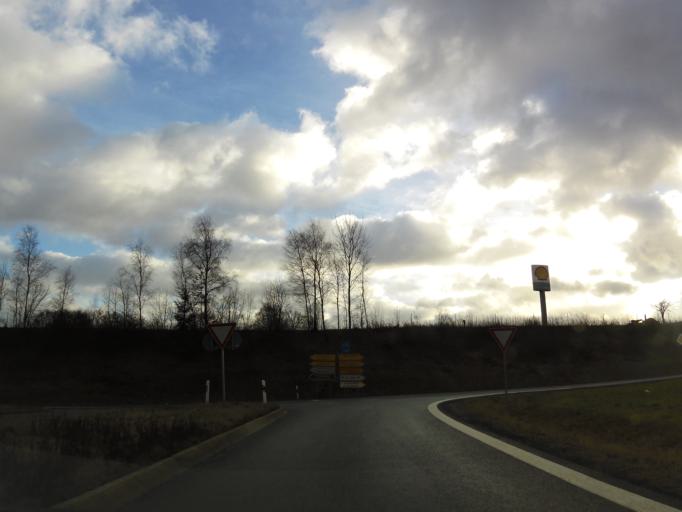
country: DE
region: Bavaria
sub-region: Upper Franconia
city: Thiersheim
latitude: 50.0749
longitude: 12.1001
